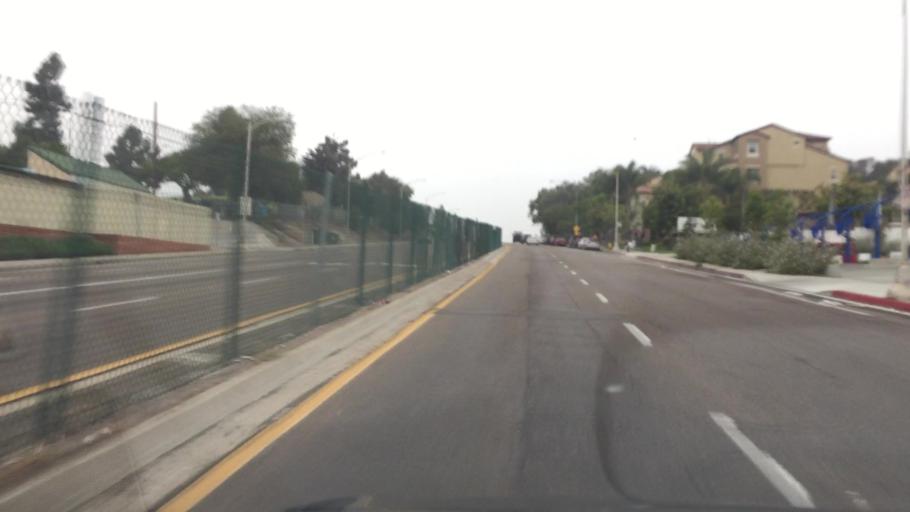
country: US
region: California
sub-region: San Diego County
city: Lemon Grove
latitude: 32.7493
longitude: -117.0794
